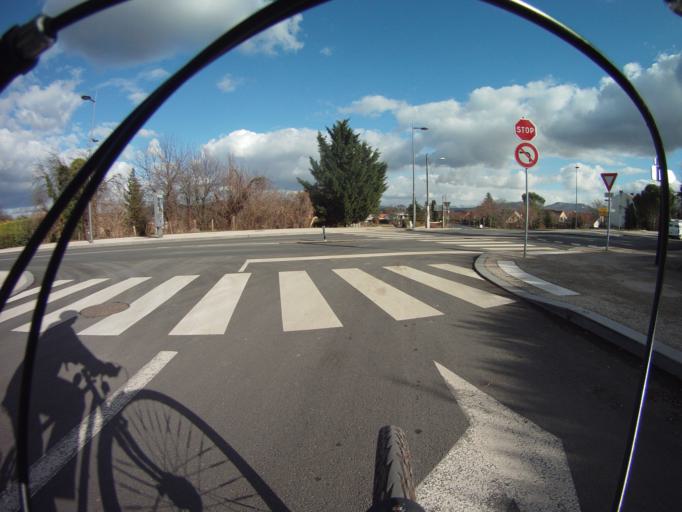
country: FR
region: Auvergne
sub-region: Departement du Puy-de-Dome
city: Perignat-les-Sarlieve
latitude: 45.7342
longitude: 3.1419
